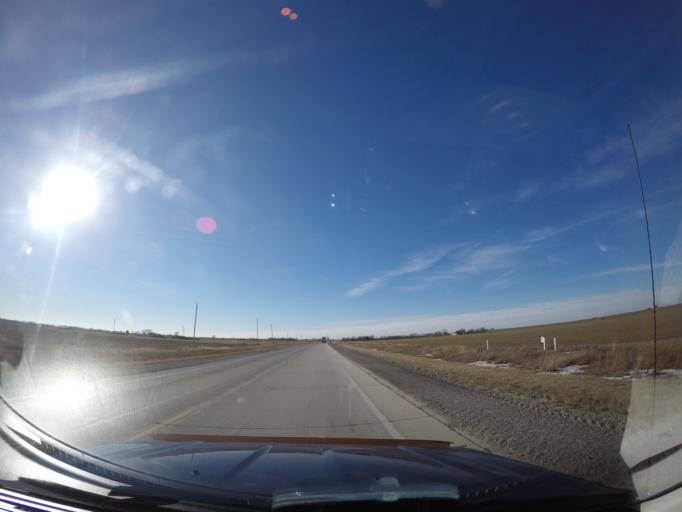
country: US
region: Kansas
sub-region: Marion County
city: Hillsboro
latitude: 38.3625
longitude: -97.1489
